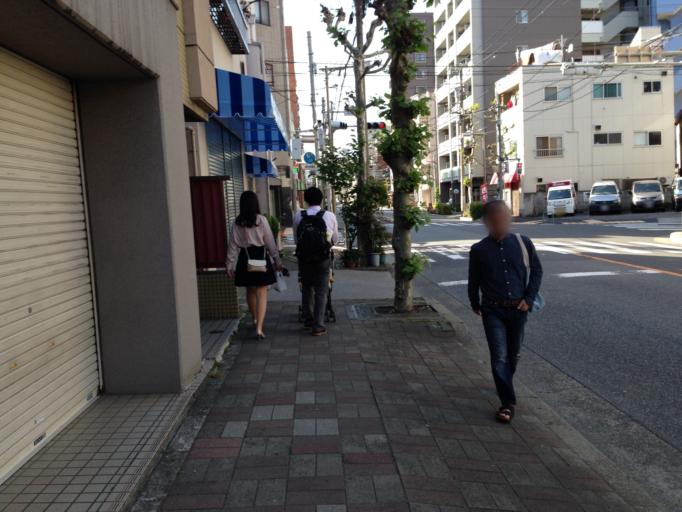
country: JP
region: Tokyo
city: Urayasu
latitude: 35.6894
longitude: 139.7933
